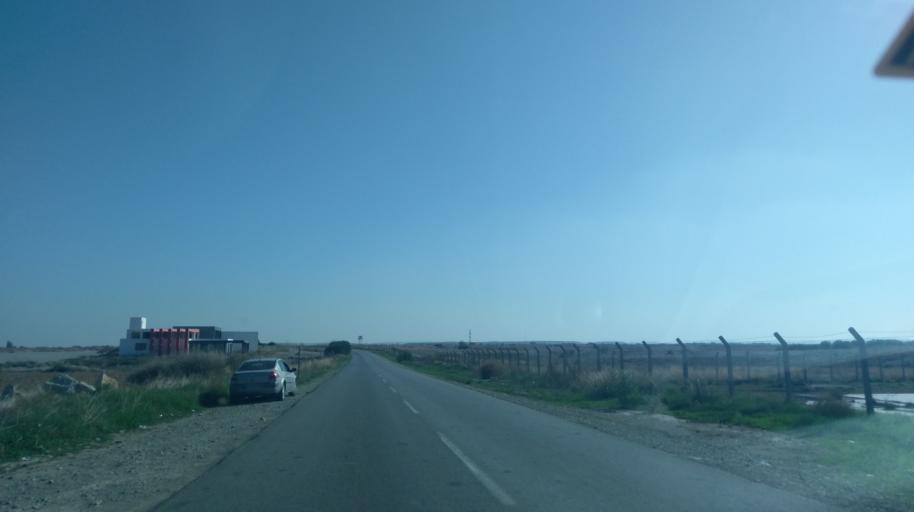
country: CY
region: Larnaka
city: Athienou
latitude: 35.1572
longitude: 33.5081
